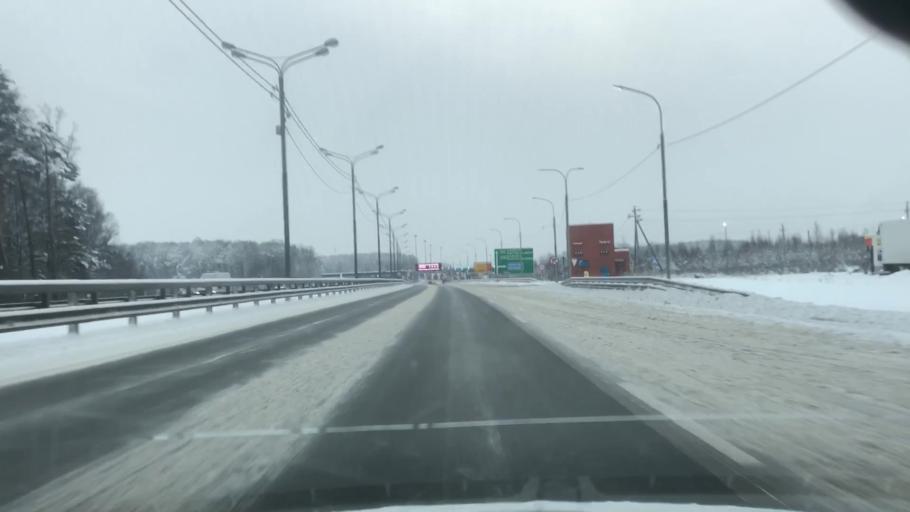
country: RU
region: Moskovskaya
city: Mikhnevo
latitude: 55.1735
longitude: 37.9127
